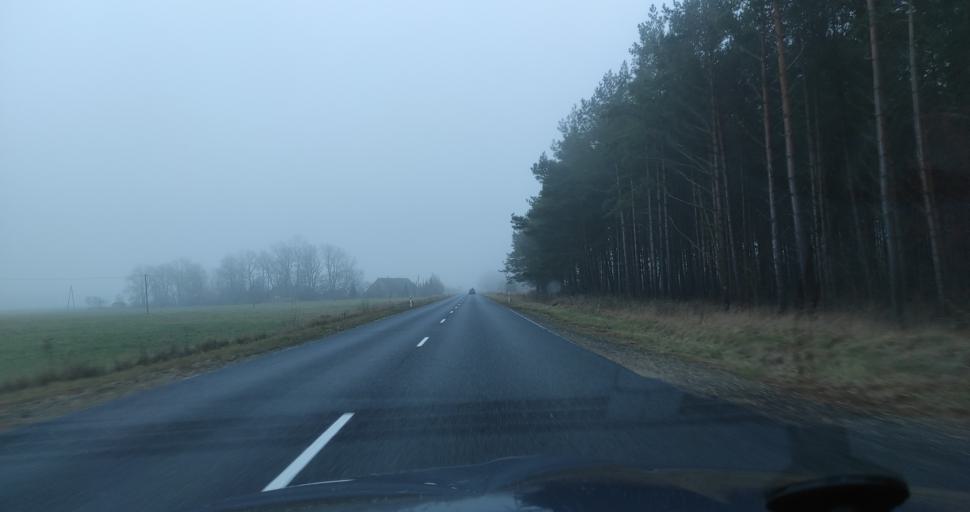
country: LV
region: Alsunga
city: Alsunga
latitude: 57.1040
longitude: 21.4228
